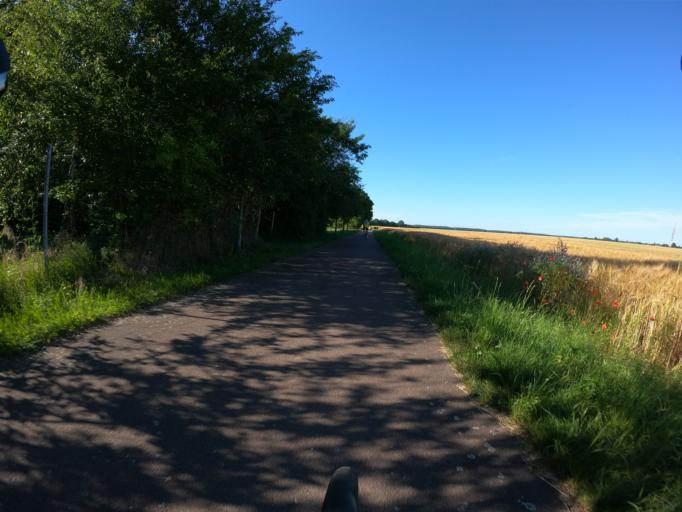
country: DE
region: Brandenburg
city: Juterbog
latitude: 52.0221
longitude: 13.0611
